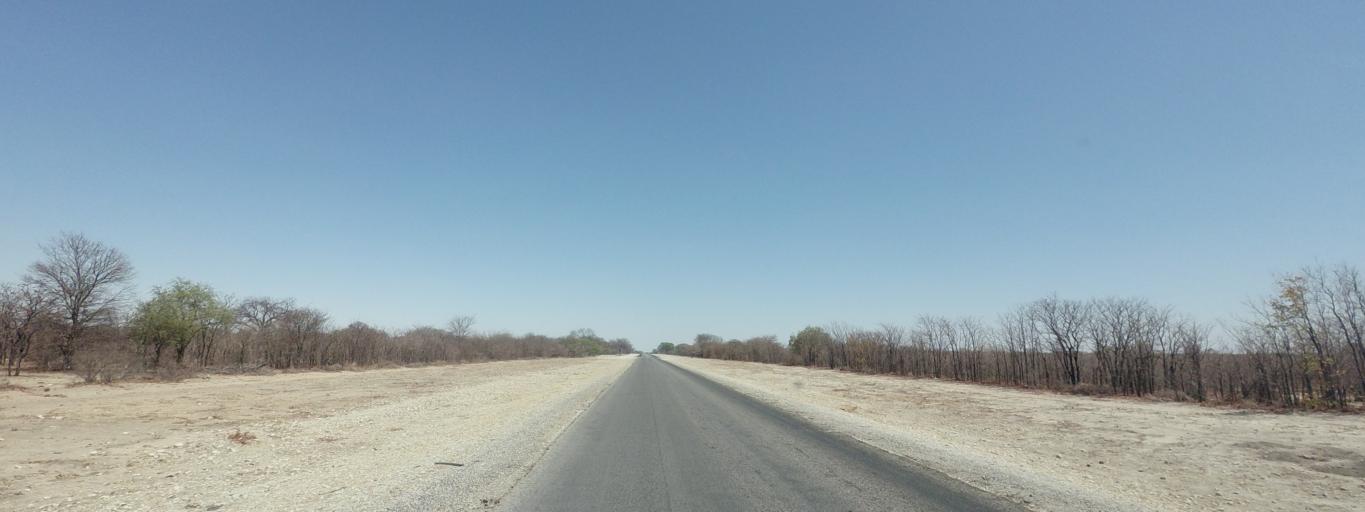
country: BW
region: North East
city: Dukwe
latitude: -20.3903
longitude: 26.3441
